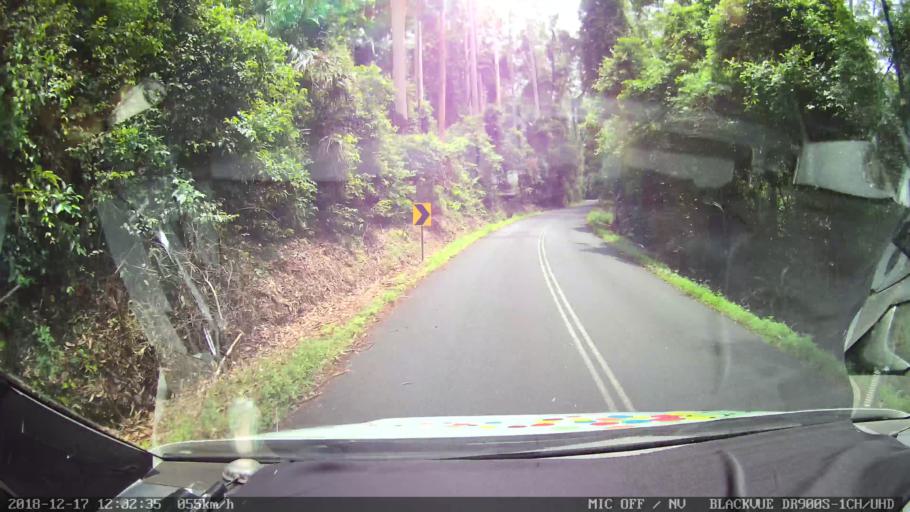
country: AU
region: New South Wales
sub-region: Kyogle
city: Kyogle
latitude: -28.5148
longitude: 152.5686
